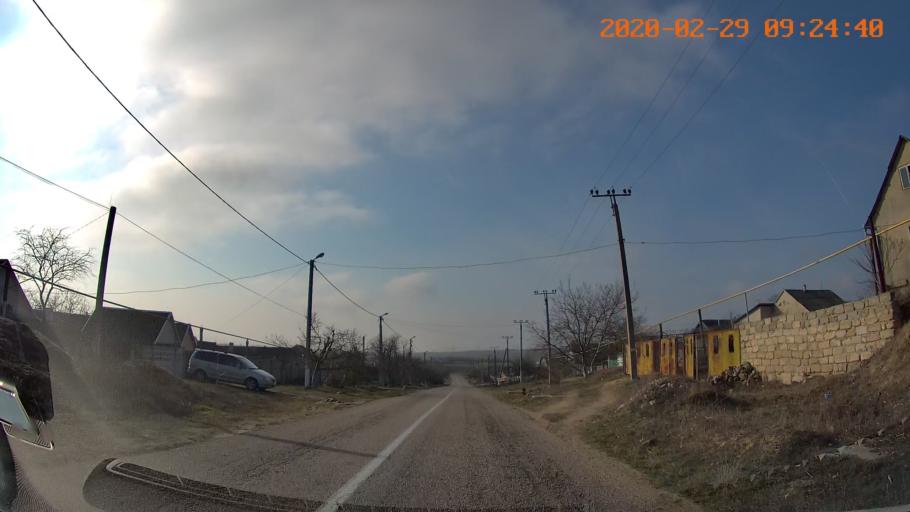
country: MD
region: Telenesti
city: Pervomaisc
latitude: 46.7139
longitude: 29.9580
